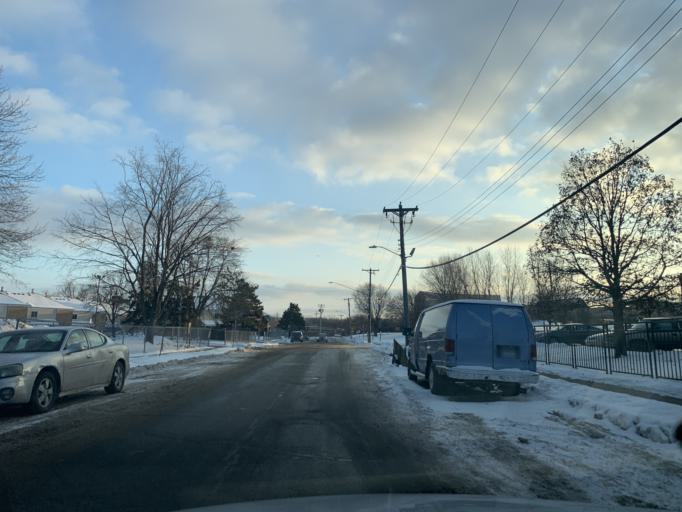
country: US
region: Minnesota
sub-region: Hennepin County
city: Minneapolis
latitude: 44.9834
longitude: -93.2982
